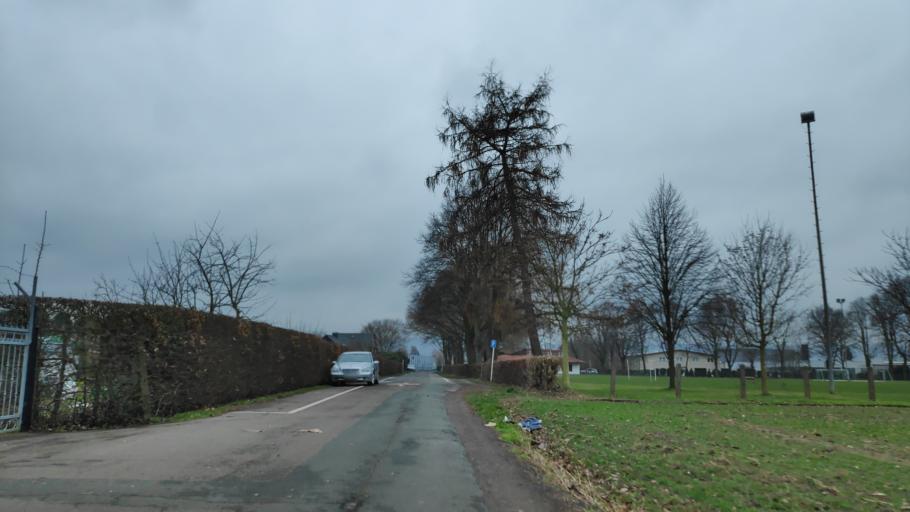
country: DE
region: North Rhine-Westphalia
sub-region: Regierungsbezirk Detmold
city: Minden
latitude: 52.2951
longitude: 8.8865
